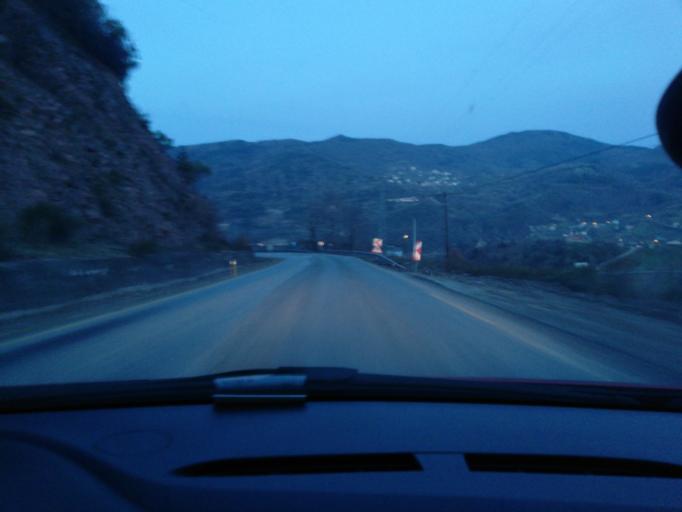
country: TR
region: Kastamonu
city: Inebolu
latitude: 41.9403
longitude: 33.7613
